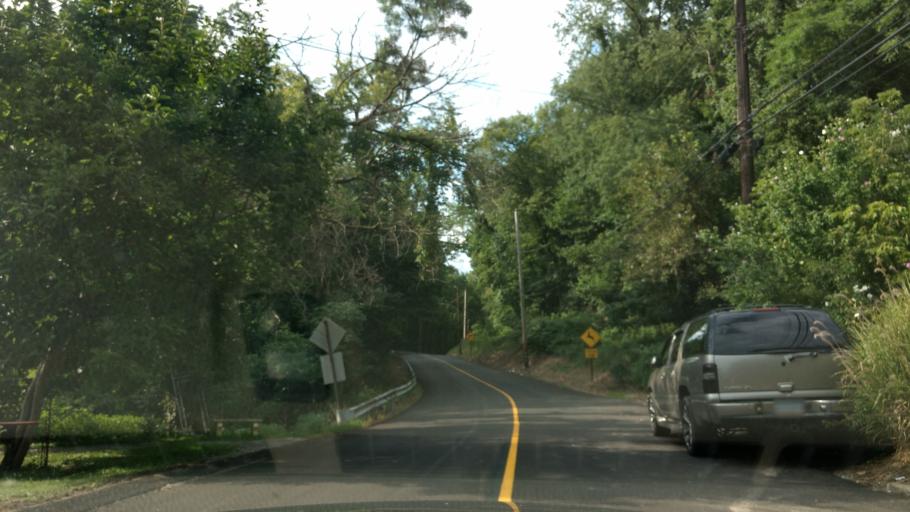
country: US
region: Pennsylvania
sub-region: Allegheny County
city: Bellevue
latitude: 40.4959
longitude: -80.0446
